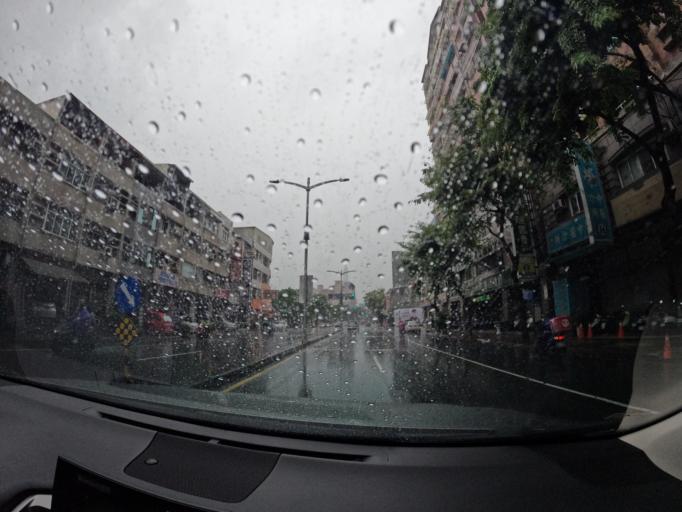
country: TW
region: Kaohsiung
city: Kaohsiung
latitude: 22.6642
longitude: 120.3218
